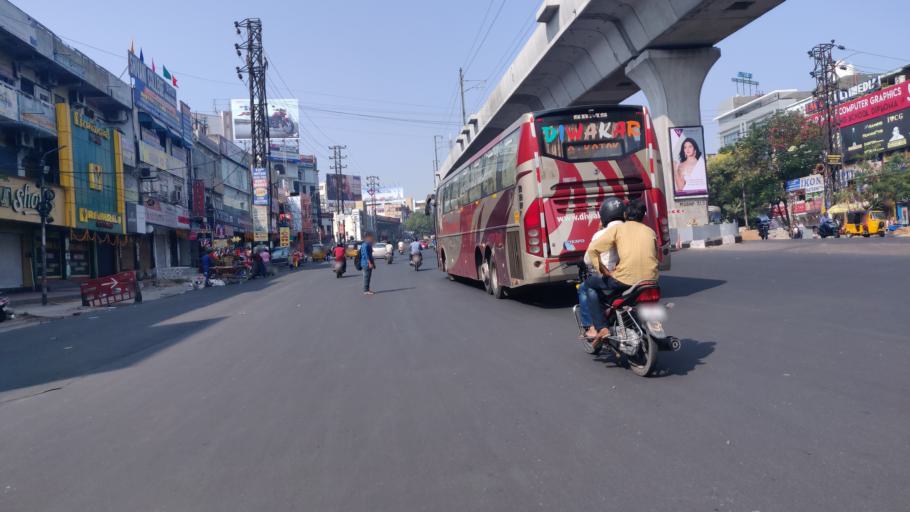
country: IN
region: Telangana
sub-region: Rangareddi
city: Gaddi Annaram
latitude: 17.3685
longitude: 78.5213
